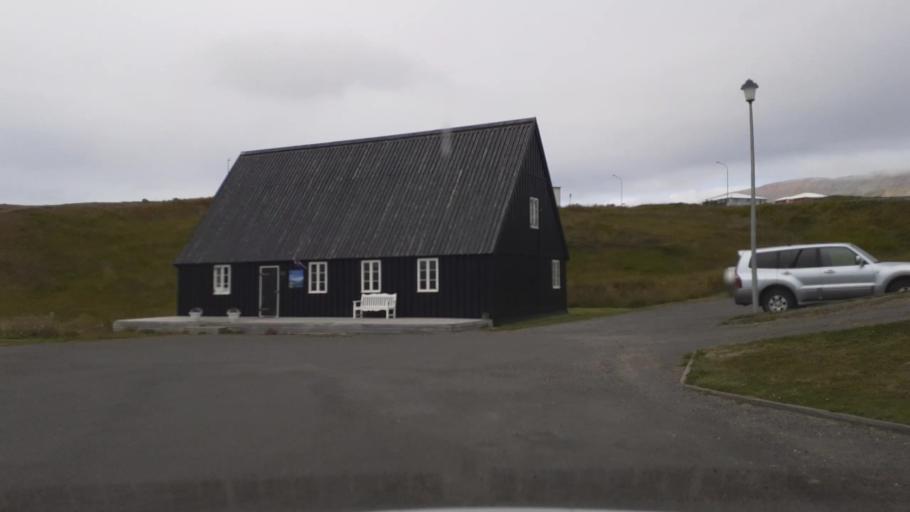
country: IS
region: Northwest
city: Saudarkrokur
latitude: 65.8989
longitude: -19.4167
